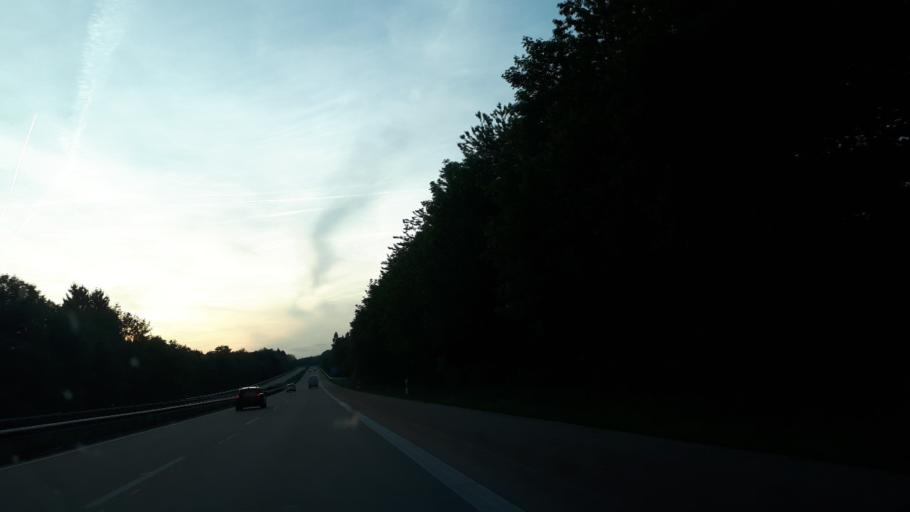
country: DE
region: Rheinland-Pfalz
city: Laubach
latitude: 50.2289
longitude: 7.0964
